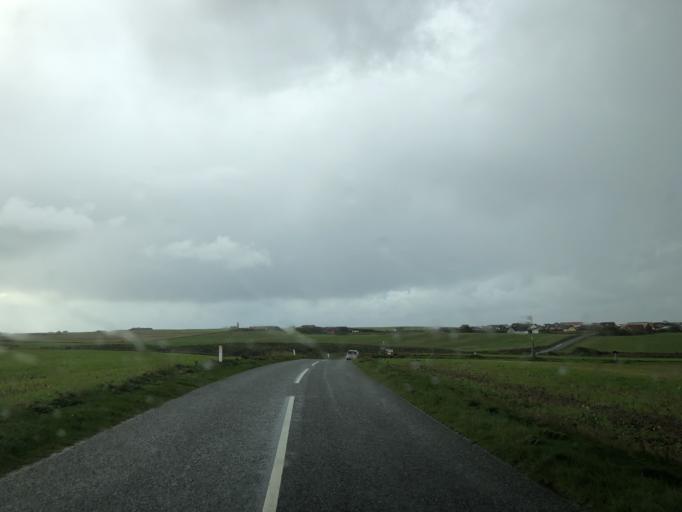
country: DK
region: Central Jutland
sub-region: Lemvig Kommune
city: Harboore
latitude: 56.5302
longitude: 8.1325
